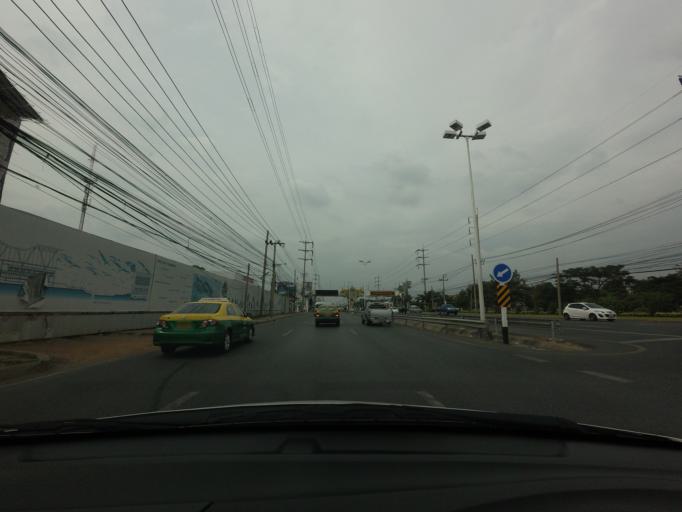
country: TH
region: Samut Prakan
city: Samut Prakan
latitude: 13.5439
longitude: 100.6188
